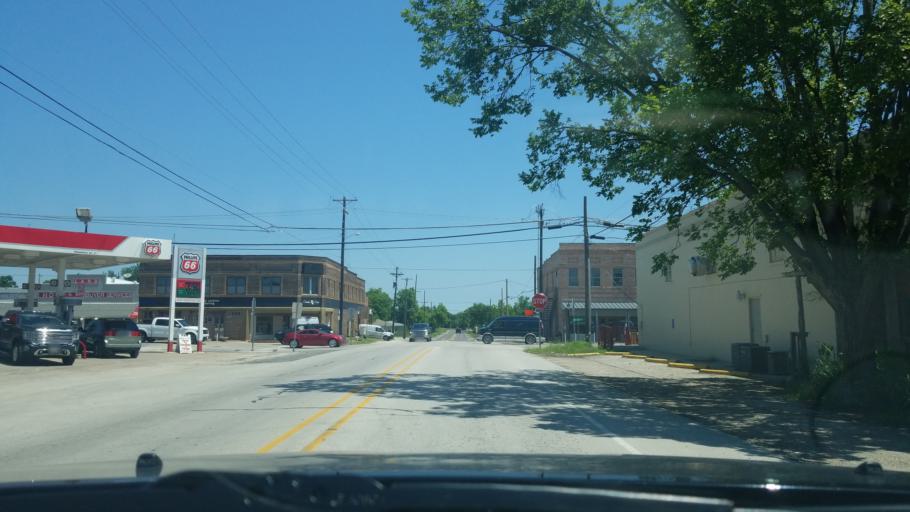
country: US
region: Texas
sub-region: Denton County
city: Krum
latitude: 33.2611
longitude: -97.2384
